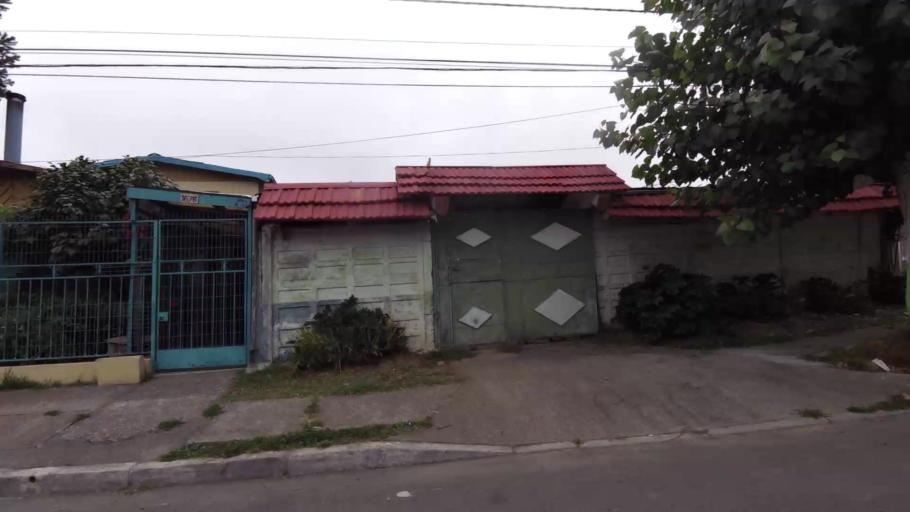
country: CL
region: Biobio
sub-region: Provincia de Concepcion
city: Concepcion
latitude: -36.8279
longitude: -73.0075
